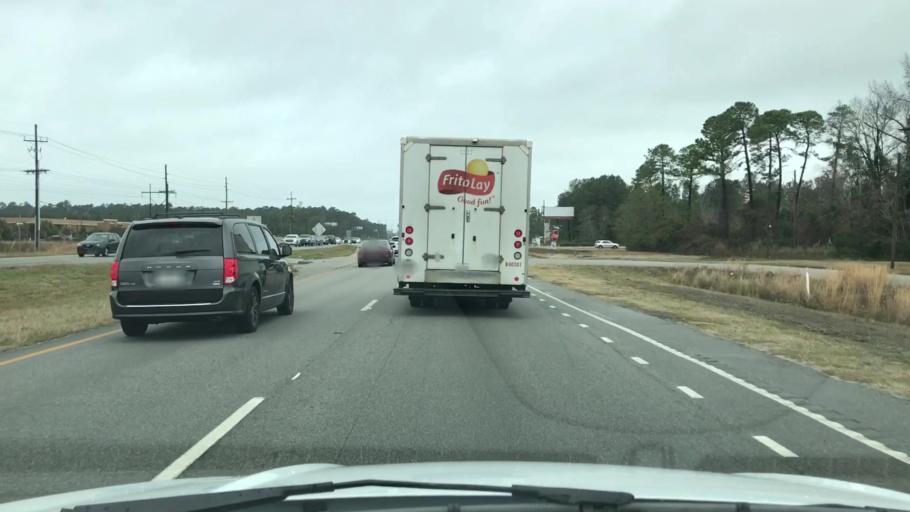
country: US
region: South Carolina
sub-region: Horry County
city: Red Hill
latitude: 33.7773
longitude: -78.9848
